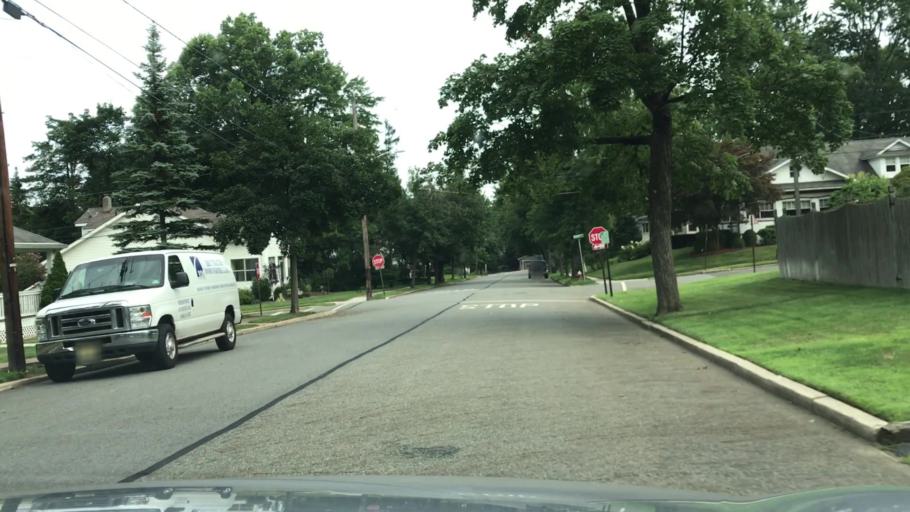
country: US
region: New Jersey
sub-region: Bergen County
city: Westwood
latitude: 40.9892
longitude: -74.0261
